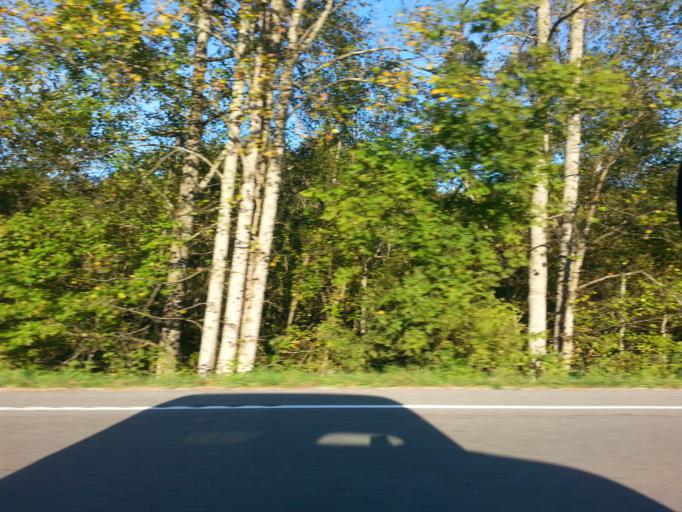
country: US
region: Tennessee
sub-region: Blount County
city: Wildwood
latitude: 35.7111
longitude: -83.8185
